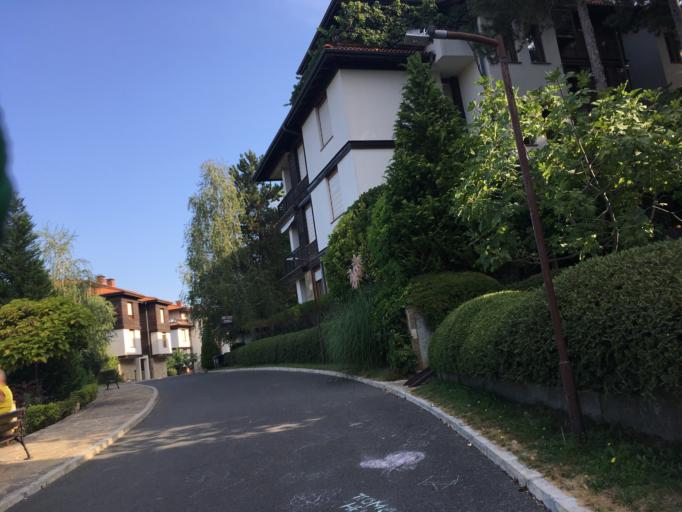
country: BG
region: Burgas
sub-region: Obshtina Sozopol
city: Sozopol
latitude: 42.4088
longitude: 27.6782
